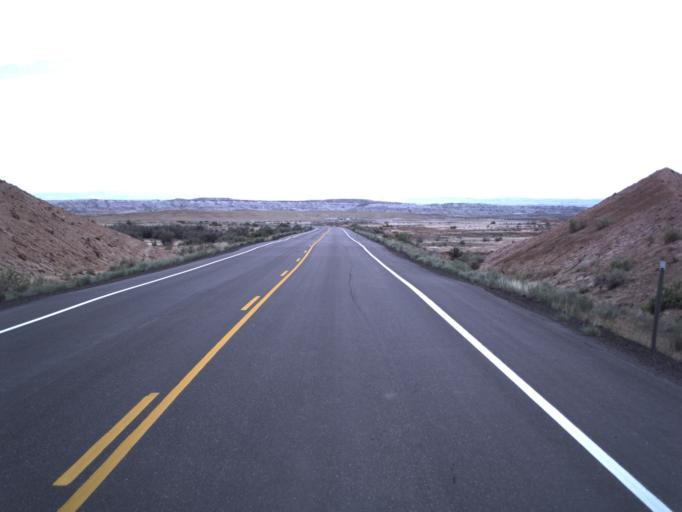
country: US
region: Utah
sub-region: Uintah County
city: Naples
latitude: 40.1251
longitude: -109.2595
